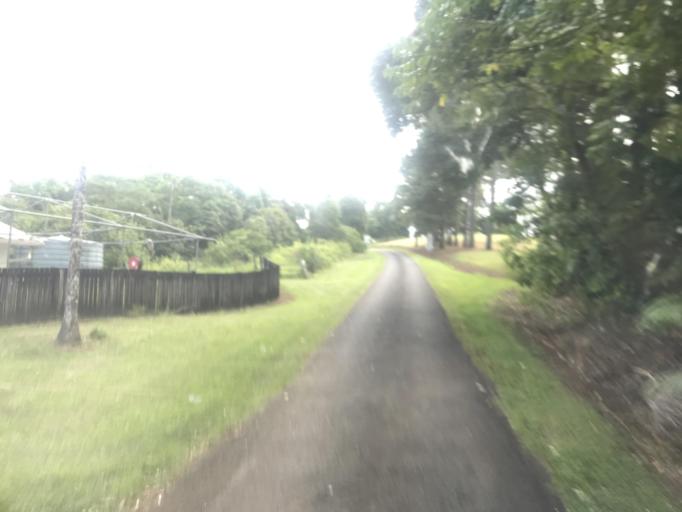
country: AU
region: Queensland
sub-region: Tablelands
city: Ravenshoe
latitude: -17.5517
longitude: 145.6967
